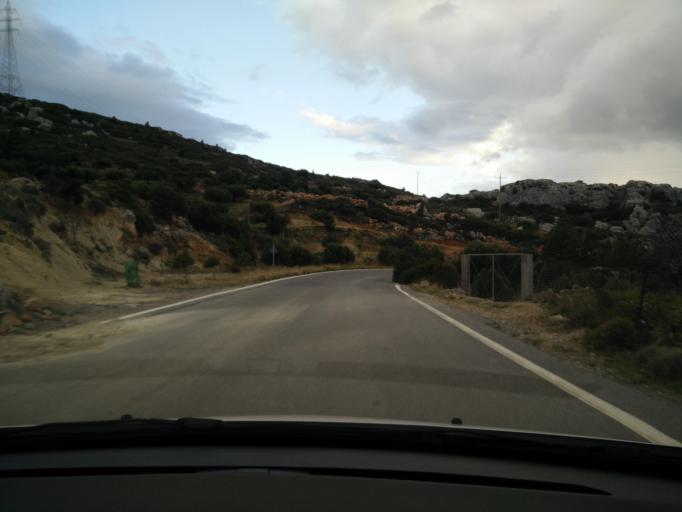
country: GR
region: Crete
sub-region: Nomos Lasithiou
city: Gra Liyia
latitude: 35.0750
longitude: 25.7037
